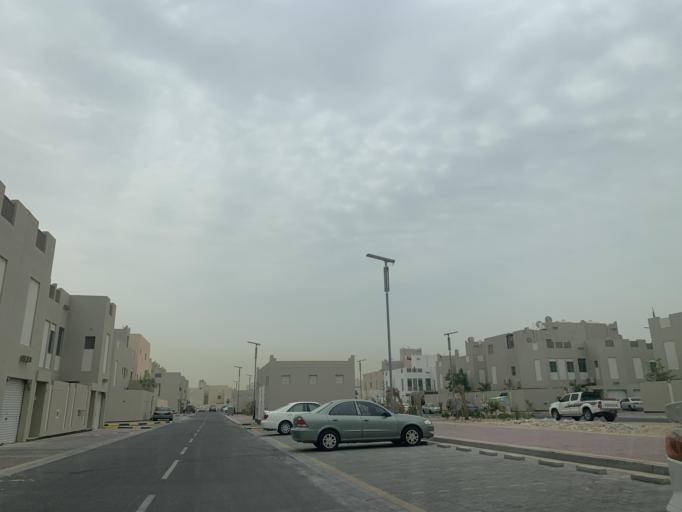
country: BH
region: Northern
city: Madinat `Isa
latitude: 26.1790
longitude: 50.5159
